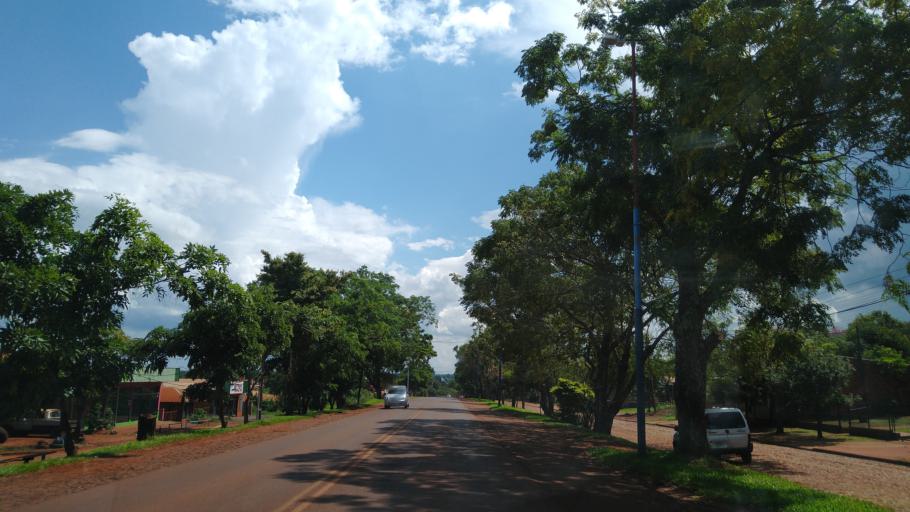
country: AR
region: Misiones
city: Puerto Libertad
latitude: -25.9702
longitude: -54.5750
